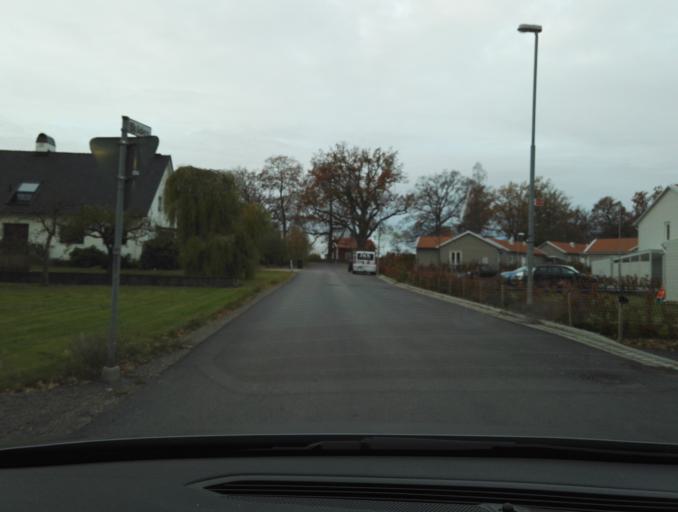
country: SE
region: Kronoberg
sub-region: Vaxjo Kommun
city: Vaexjoe
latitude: 56.9125
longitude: 14.7389
